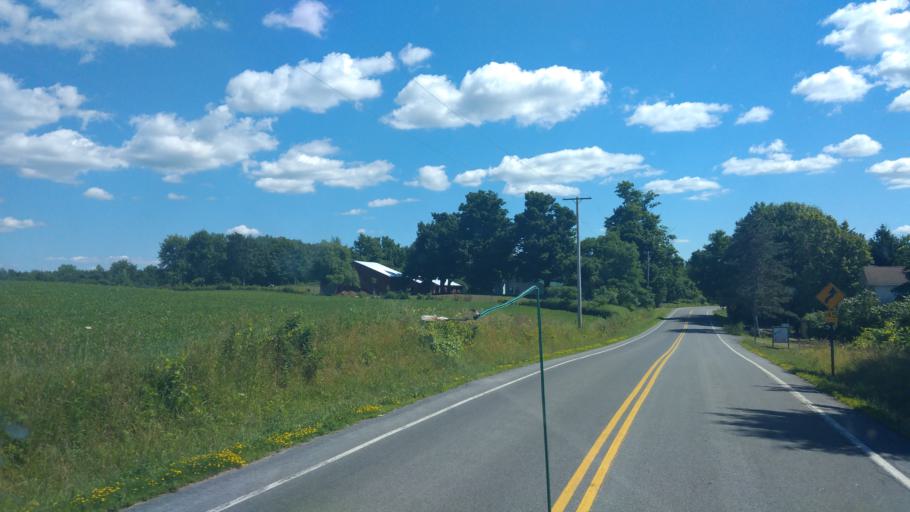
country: US
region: New York
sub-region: Wayne County
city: Sodus
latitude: 43.1599
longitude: -77.0121
